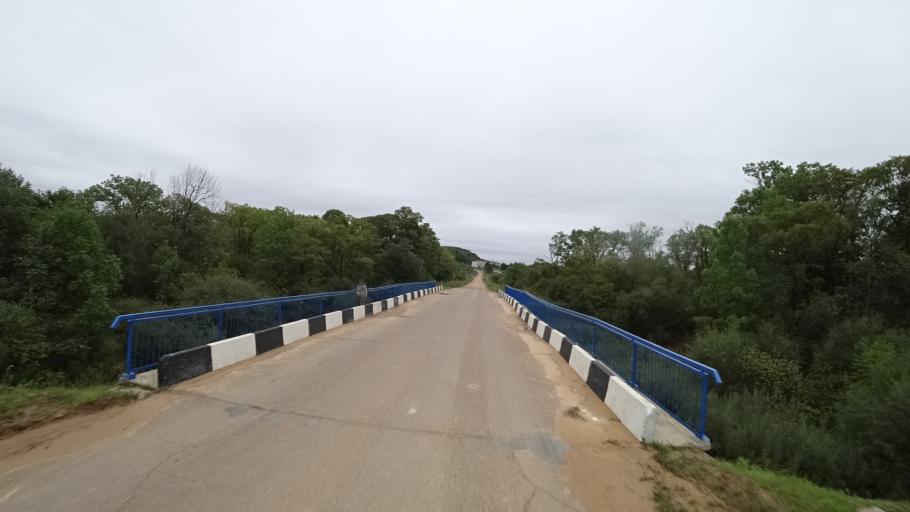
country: RU
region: Primorskiy
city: Rettikhovka
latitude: 44.1772
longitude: 132.8763
